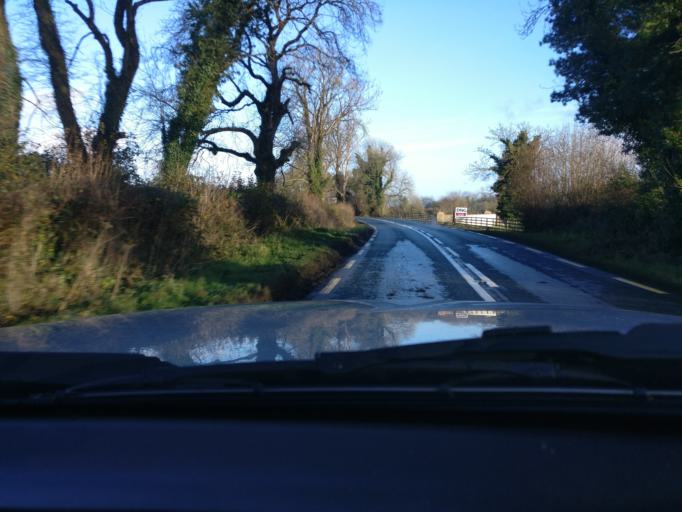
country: IE
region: Leinster
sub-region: An Mhi
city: Athboy
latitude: 53.6379
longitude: -7.0405
